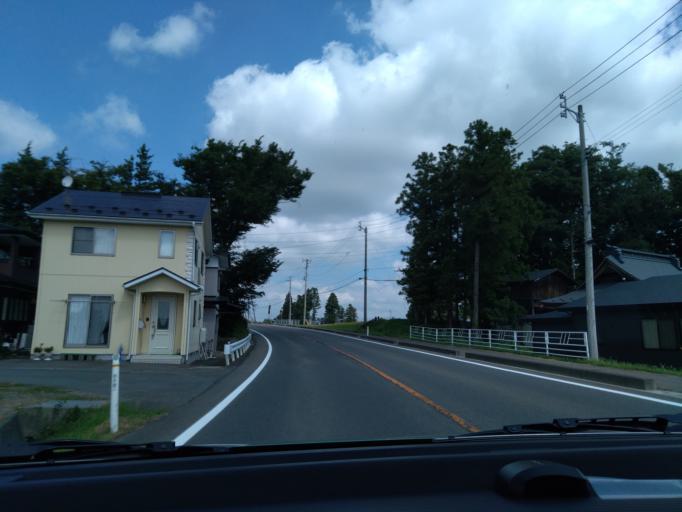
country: JP
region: Iwate
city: Hanamaki
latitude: 39.4265
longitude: 141.0889
